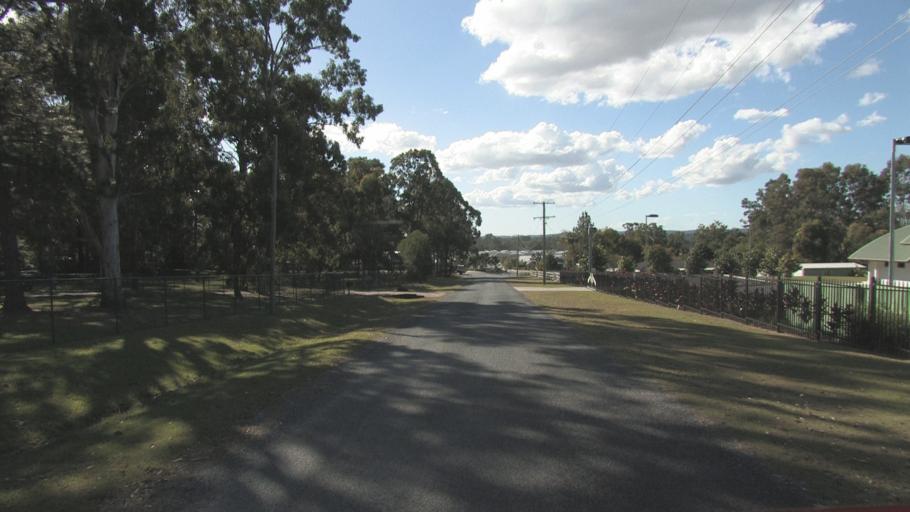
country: AU
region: Queensland
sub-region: Logan
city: Logan Reserve
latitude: -27.7148
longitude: 153.1112
